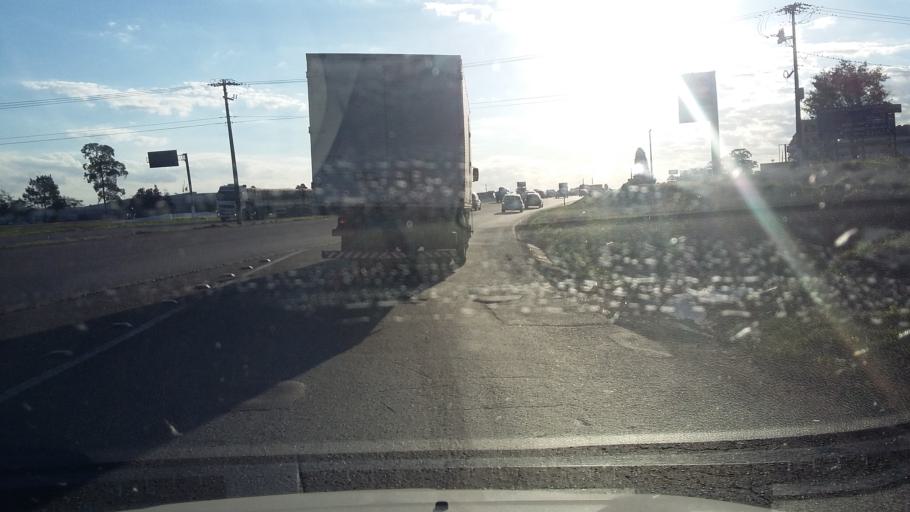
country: BR
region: Parana
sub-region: Sao Jose Dos Pinhais
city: Sao Jose dos Pinhais
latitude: -25.5429
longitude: -49.3077
